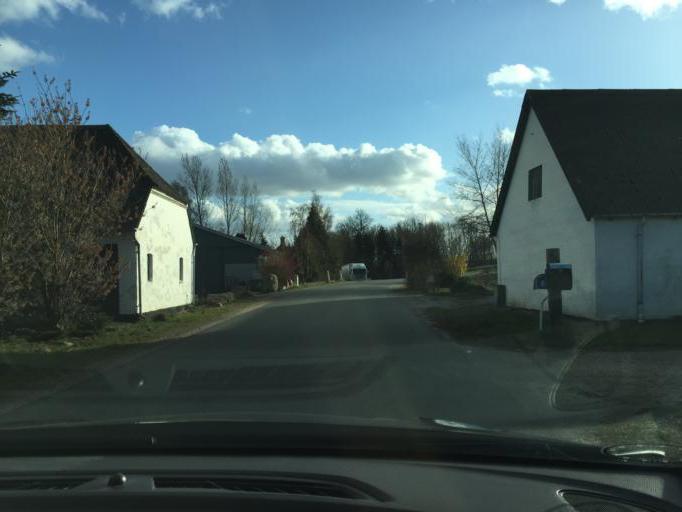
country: DK
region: South Denmark
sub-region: Nyborg Kommune
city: Ullerslev
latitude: 55.3593
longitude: 10.6292
